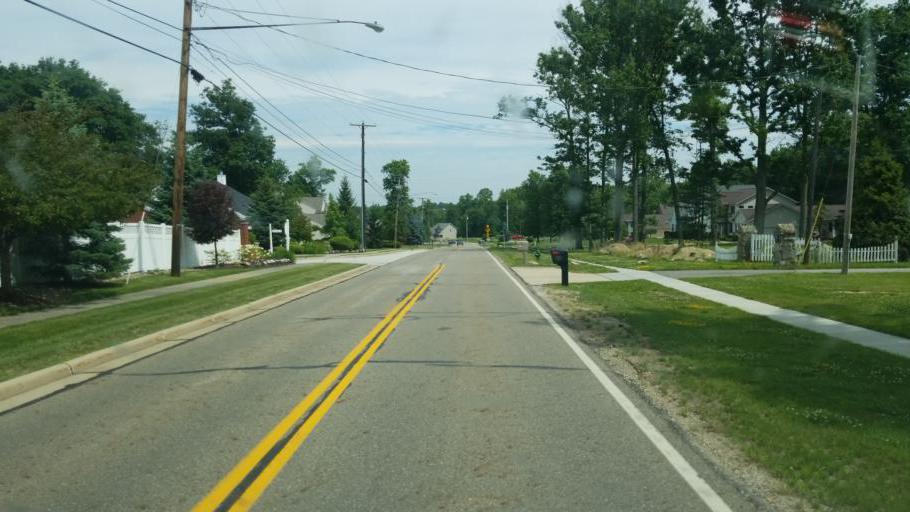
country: US
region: Ohio
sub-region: Summit County
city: Twinsburg
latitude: 41.3159
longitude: -81.4723
